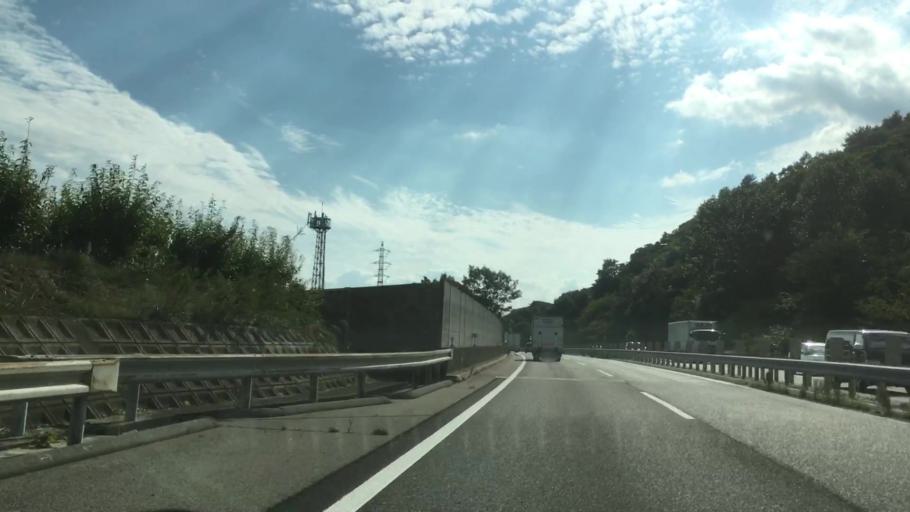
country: JP
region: Hiroshima
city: Ono-hara
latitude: 34.2839
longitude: 132.2611
